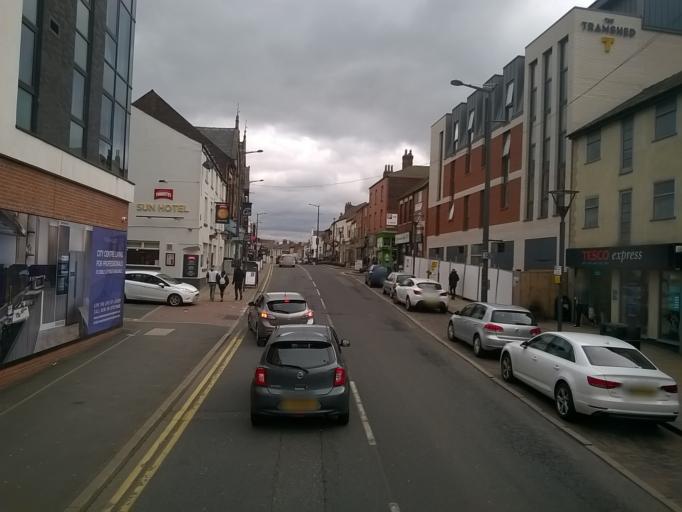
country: GB
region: England
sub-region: Lancashire
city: Preston
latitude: 53.7617
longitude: -2.7055
